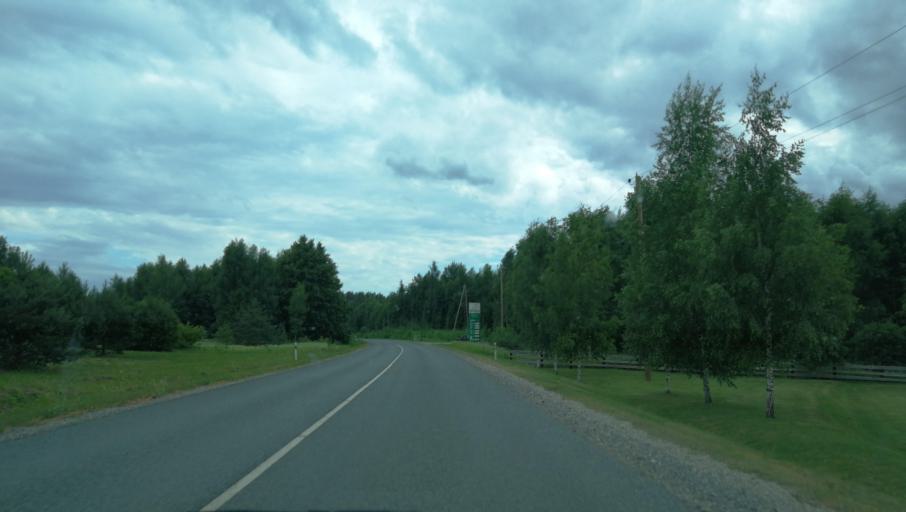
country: LV
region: Naukseni
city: Naukseni
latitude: 57.7280
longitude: 25.4222
